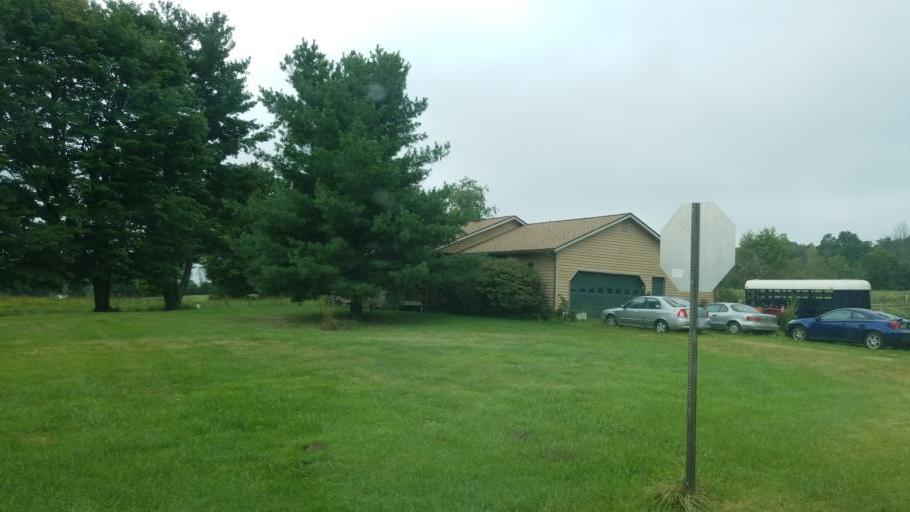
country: US
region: Ohio
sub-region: Licking County
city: Utica
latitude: 40.2734
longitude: -82.3904
